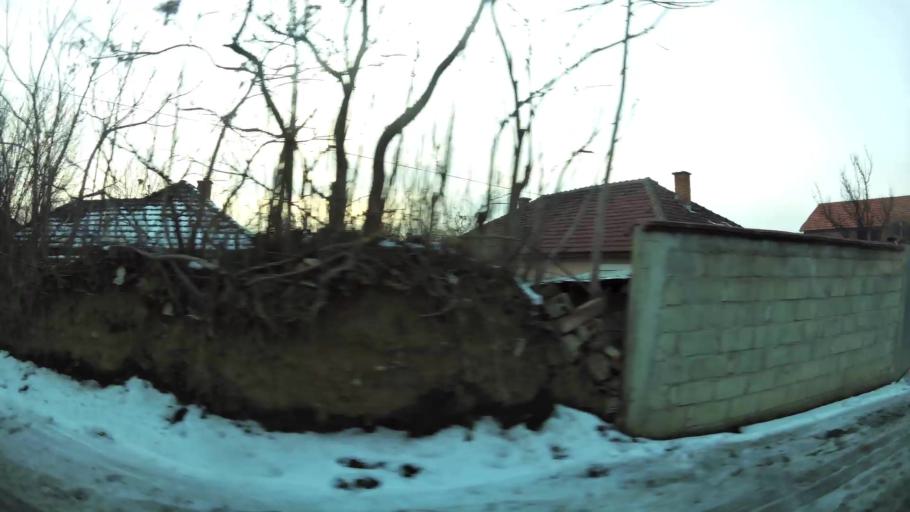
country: MK
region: Aracinovo
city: Arachinovo
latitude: 42.0221
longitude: 21.5591
